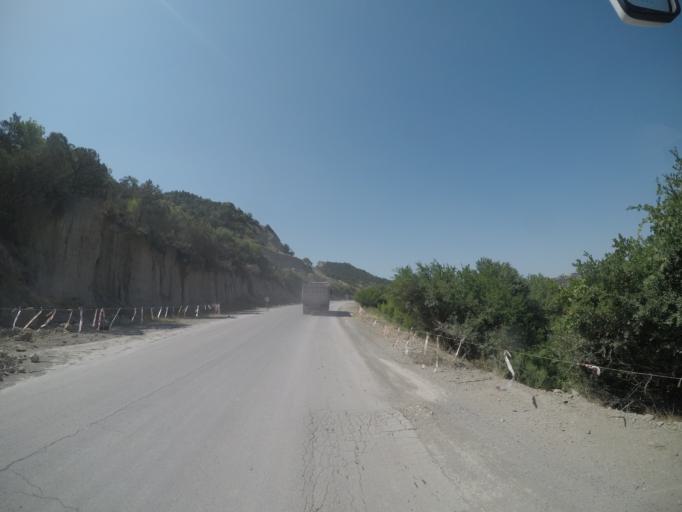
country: AZ
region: Agdas
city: Agdas
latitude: 40.7229
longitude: 47.5638
